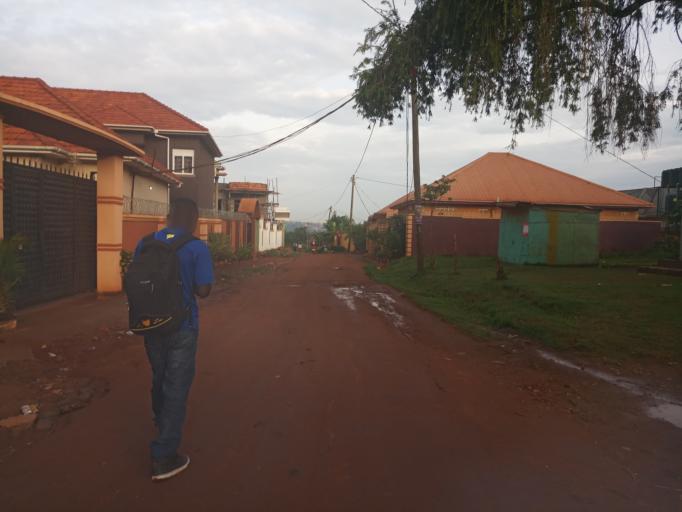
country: UG
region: Central Region
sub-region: Wakiso District
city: Kireka
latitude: 0.3935
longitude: 32.6364
